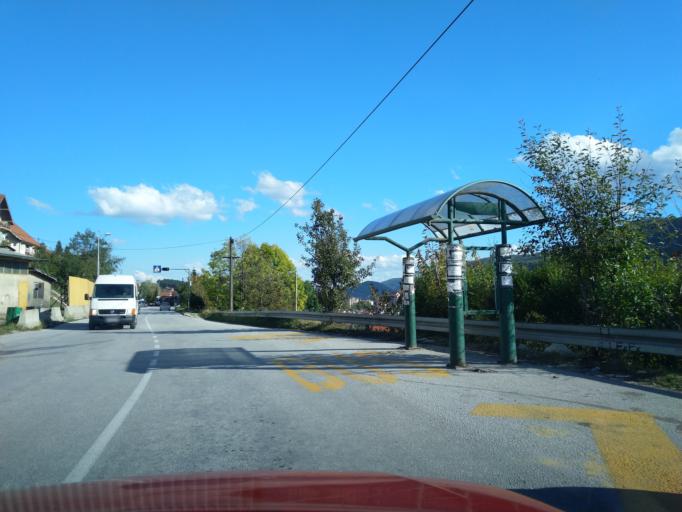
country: RS
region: Central Serbia
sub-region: Zlatiborski Okrug
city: Uzice
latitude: 43.8620
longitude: 19.8171
